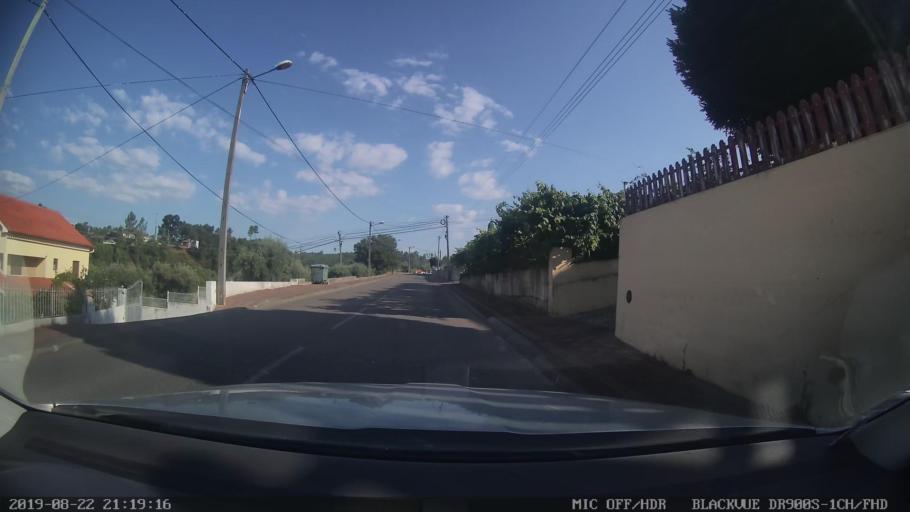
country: PT
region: Castelo Branco
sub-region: Serta
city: Serta
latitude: 39.8046
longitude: -8.1081
